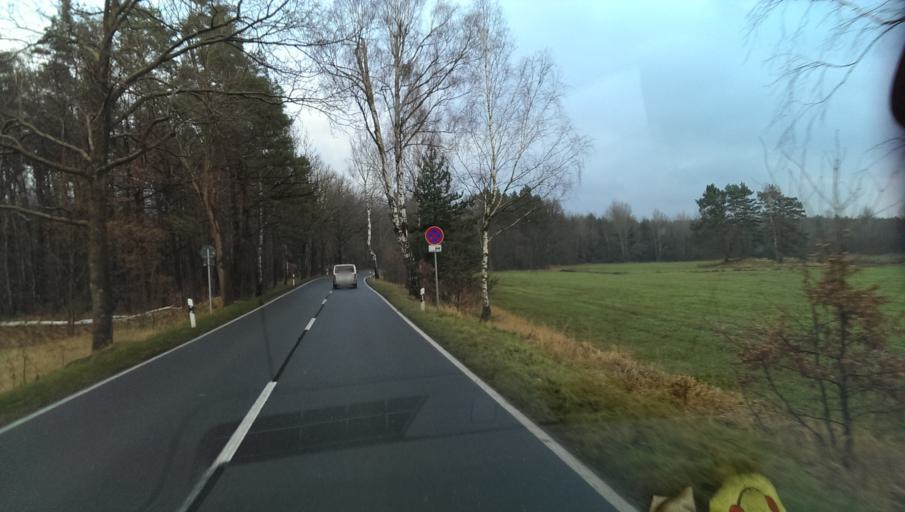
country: DE
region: Saxony
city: Weinbohla
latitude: 51.1850
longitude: 13.6122
